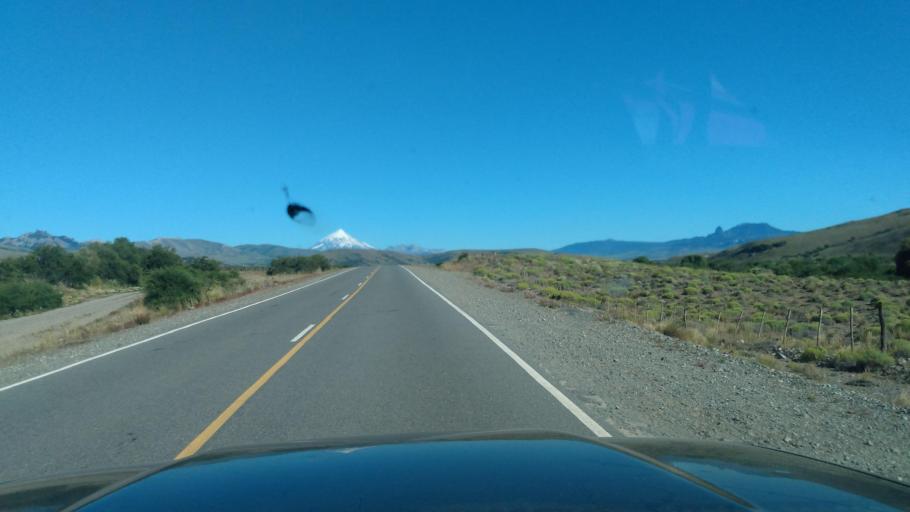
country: AR
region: Neuquen
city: Junin de los Andes
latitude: -39.8846
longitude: -71.1590
